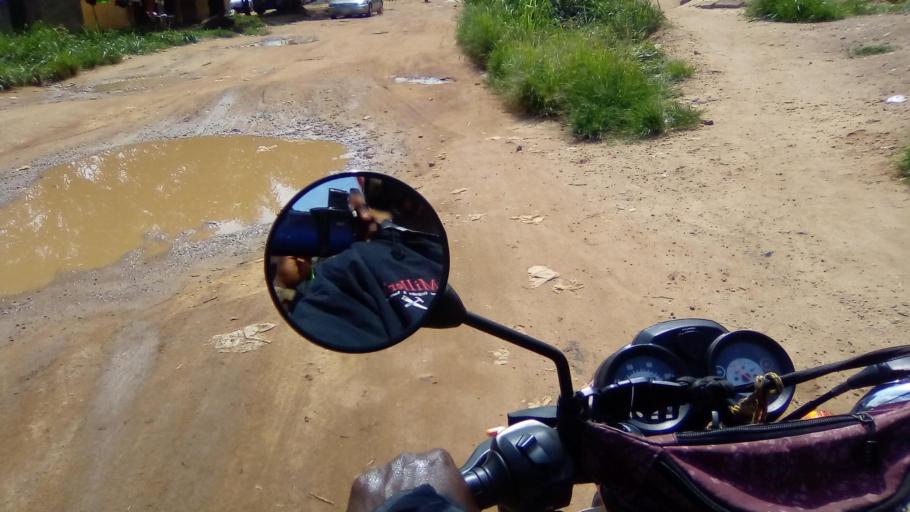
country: SL
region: Southern Province
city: Bo
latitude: 7.9503
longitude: -11.7238
